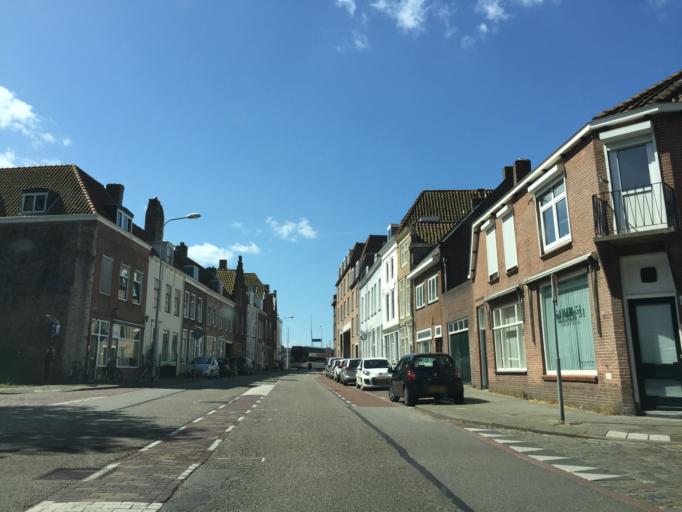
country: NL
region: Zeeland
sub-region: Gemeente Middelburg
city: Middelburg
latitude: 51.5020
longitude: 3.6235
